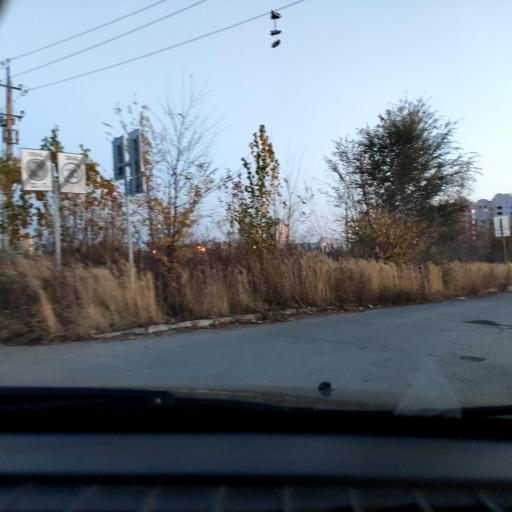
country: RU
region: Samara
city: Tol'yatti
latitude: 53.5520
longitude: 49.3253
